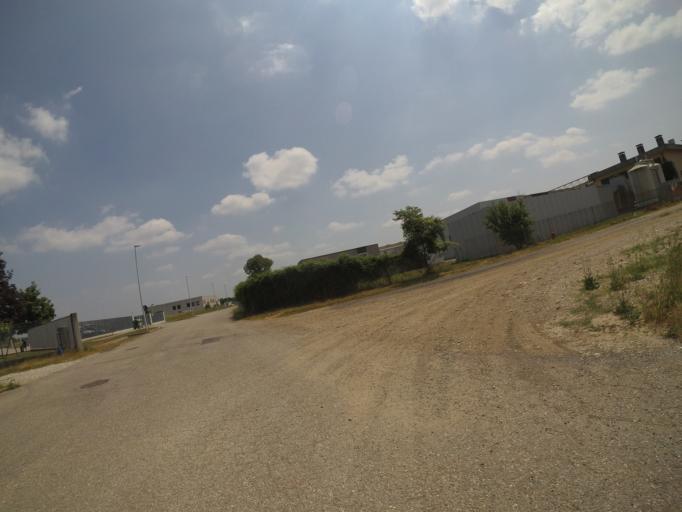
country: IT
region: Friuli Venezia Giulia
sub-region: Provincia di Udine
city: Bertiolo
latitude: 45.9510
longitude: 13.0588
